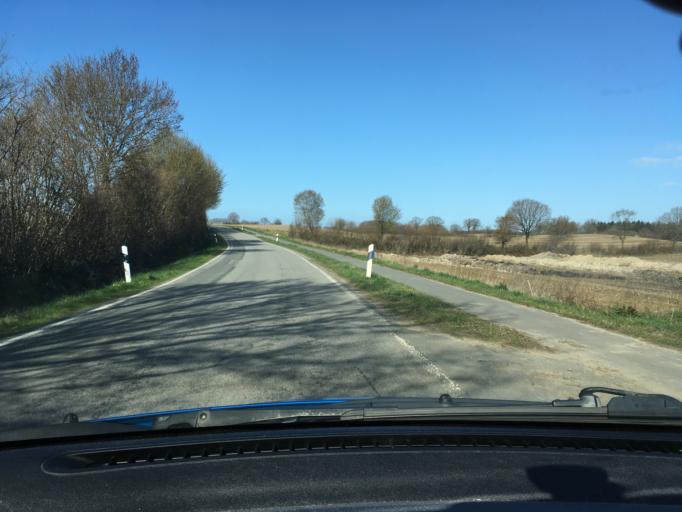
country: DE
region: Schleswig-Holstein
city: Fahrdorf
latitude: 54.5038
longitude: 9.6292
